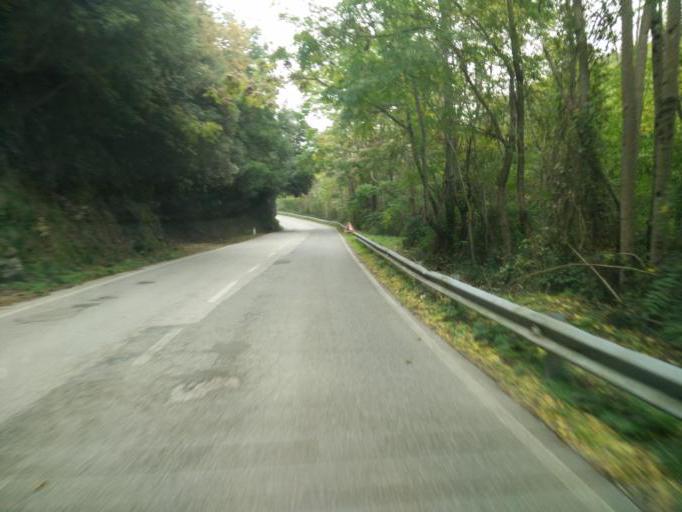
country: IT
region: Tuscany
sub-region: Provincia di Massa-Carrara
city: Casola in Lunigiana
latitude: 44.1979
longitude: 10.1604
